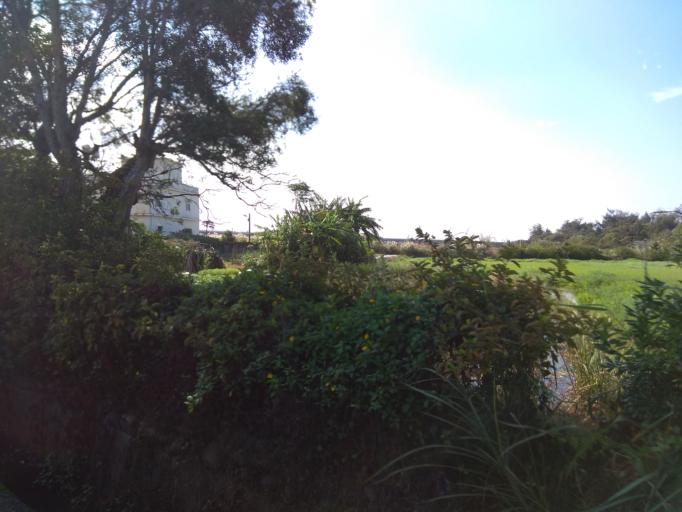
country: TW
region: Taiwan
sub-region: Hsinchu
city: Zhubei
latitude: 24.9576
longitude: 121.0040
